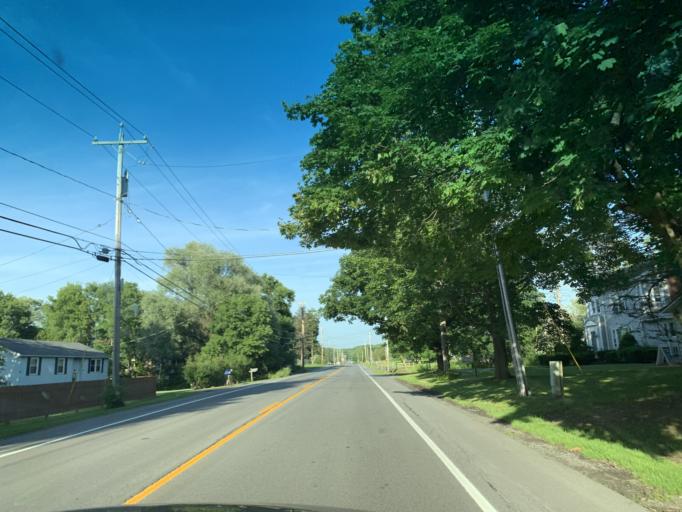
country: US
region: New York
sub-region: Oneida County
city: Clinton
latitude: 43.0703
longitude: -75.3393
